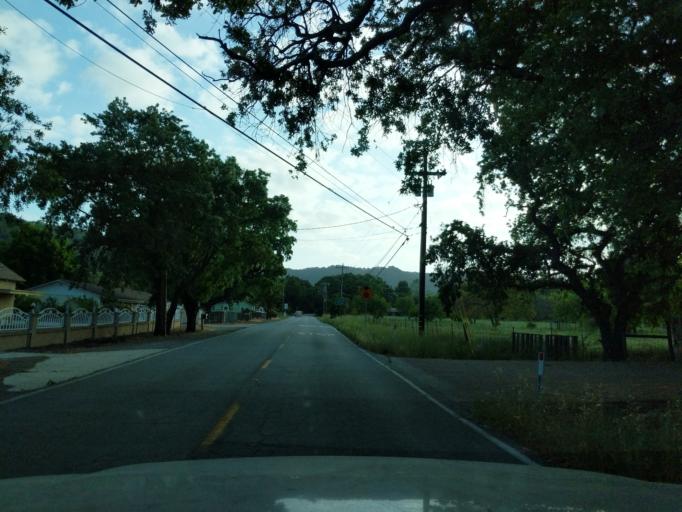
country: US
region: California
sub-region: Santa Clara County
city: Morgan Hill
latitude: 37.1072
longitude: -121.6556
